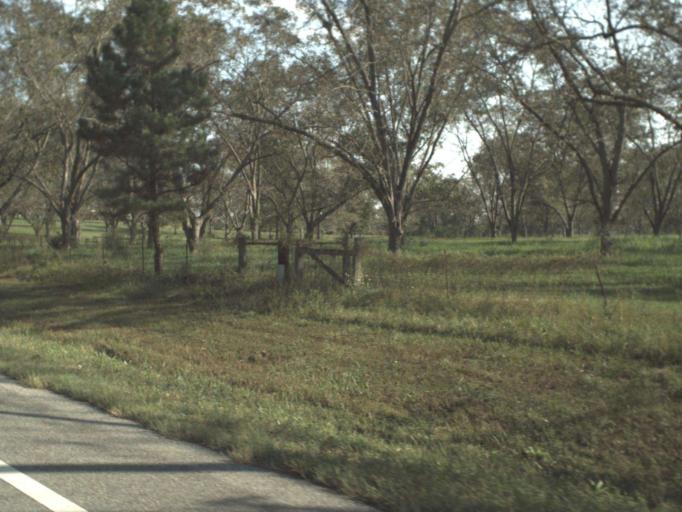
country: US
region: Florida
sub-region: Holmes County
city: Bonifay
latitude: 30.9164
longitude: -85.6494
